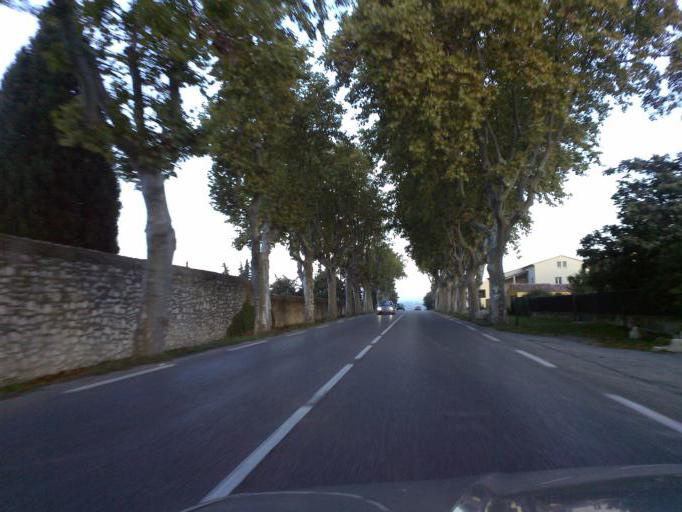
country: FR
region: Provence-Alpes-Cote d'Azur
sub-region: Departement des Bouches-du-Rhone
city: Saint-Cannat
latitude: 43.6246
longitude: 5.2940
